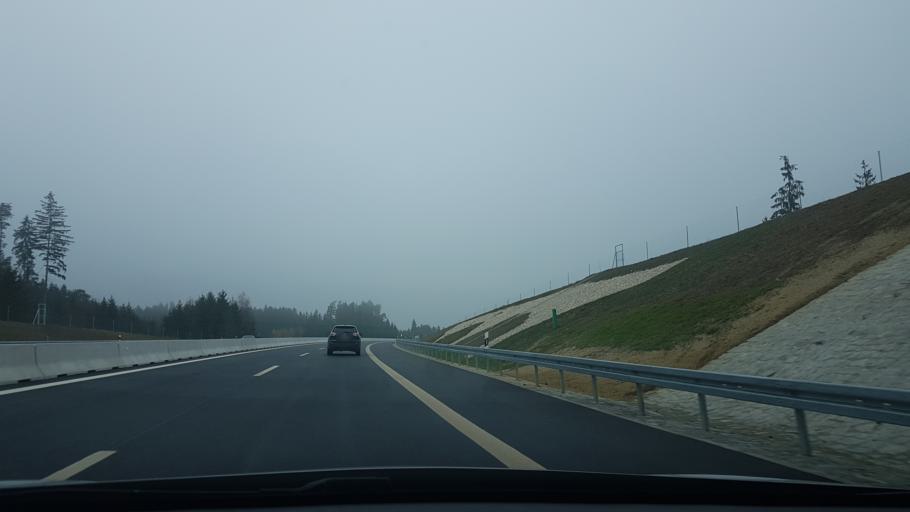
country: DE
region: Bavaria
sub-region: Lower Bavaria
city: Buch
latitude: 48.6531
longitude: 12.1891
